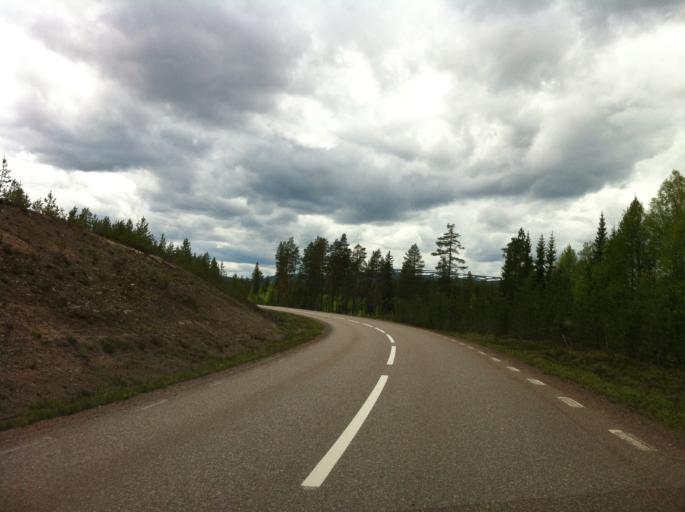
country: NO
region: Hedmark
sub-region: Trysil
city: Innbygda
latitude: 61.3799
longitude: 13.0642
